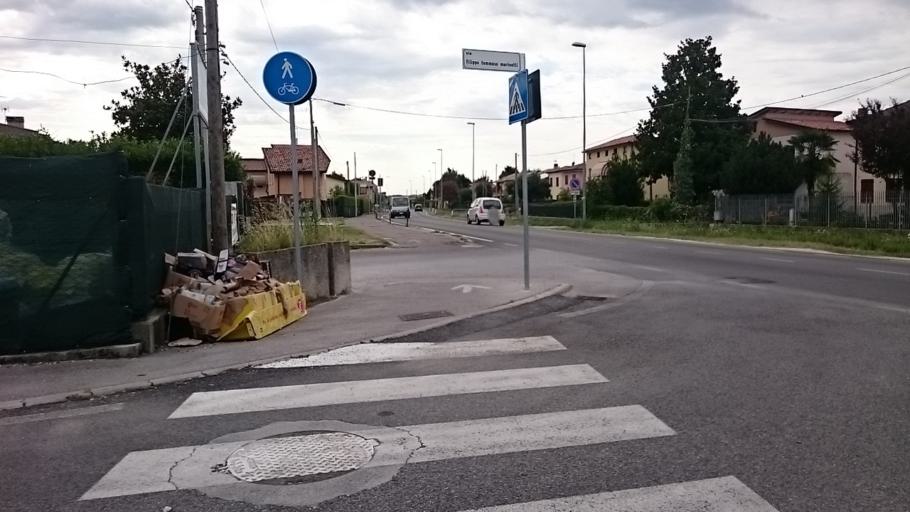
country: IT
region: Veneto
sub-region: Provincia di Padova
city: Masera di Padova
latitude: 45.3181
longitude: 11.8727
